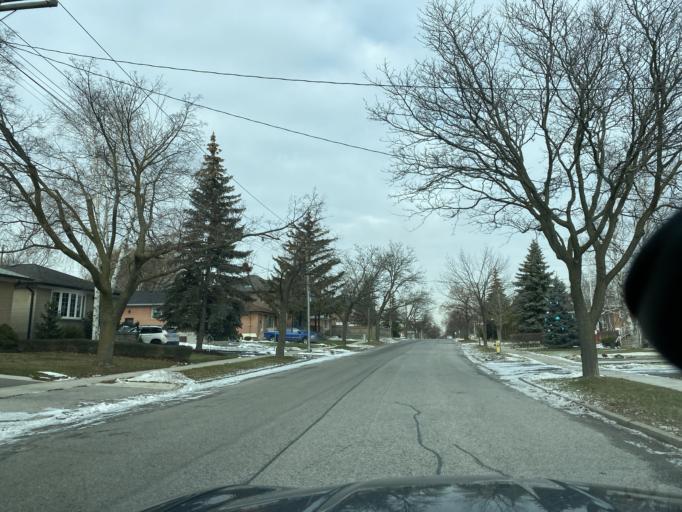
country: CA
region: Ontario
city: Etobicoke
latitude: 43.6627
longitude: -79.5768
